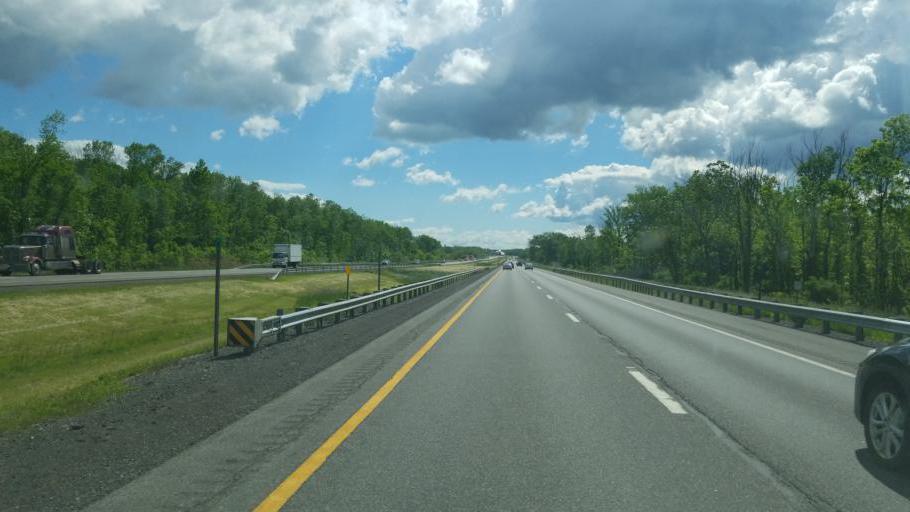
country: US
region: New York
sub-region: Madison County
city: Bolivar
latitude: 43.0954
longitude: -75.8645
